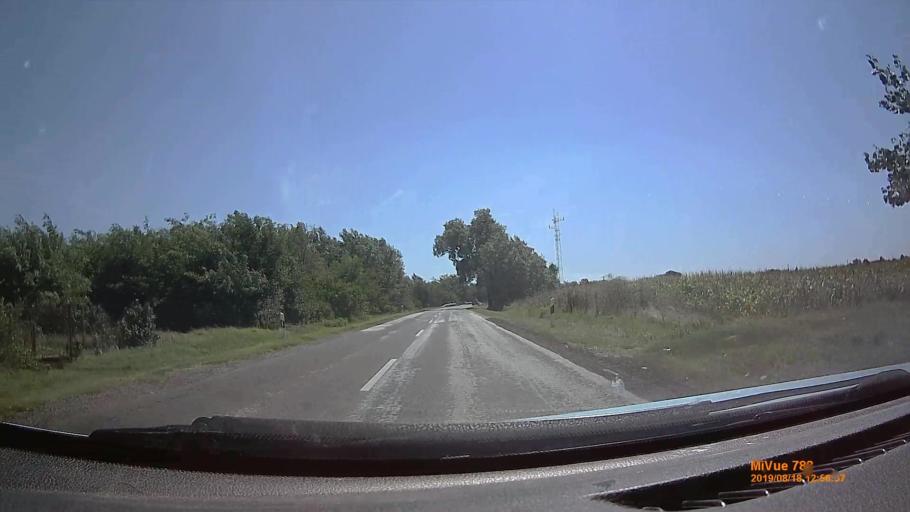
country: HU
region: Fejer
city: Sarkeresztur
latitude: 47.0190
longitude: 18.5440
